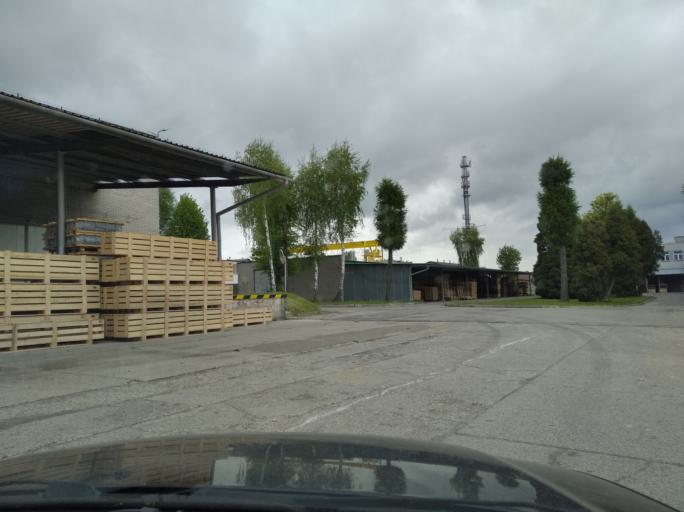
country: PL
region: Subcarpathian Voivodeship
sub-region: Powiat rzeszowski
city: Boguchwala
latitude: 49.9850
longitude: 21.9344
